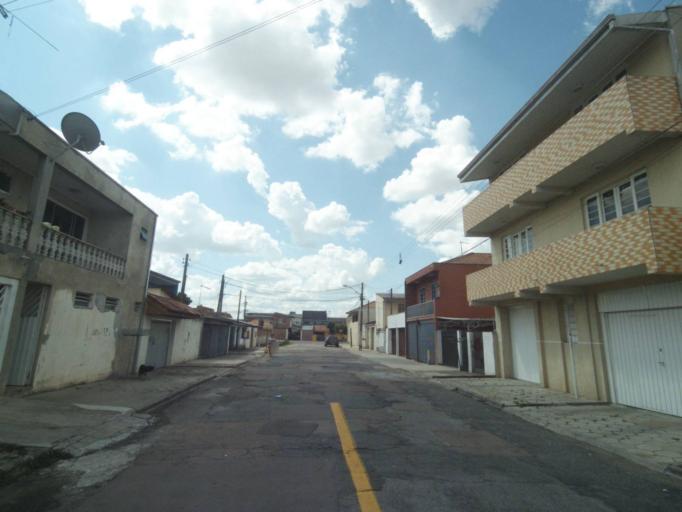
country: BR
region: Parana
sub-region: Sao Jose Dos Pinhais
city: Sao Jose dos Pinhais
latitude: -25.5336
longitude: -49.2594
